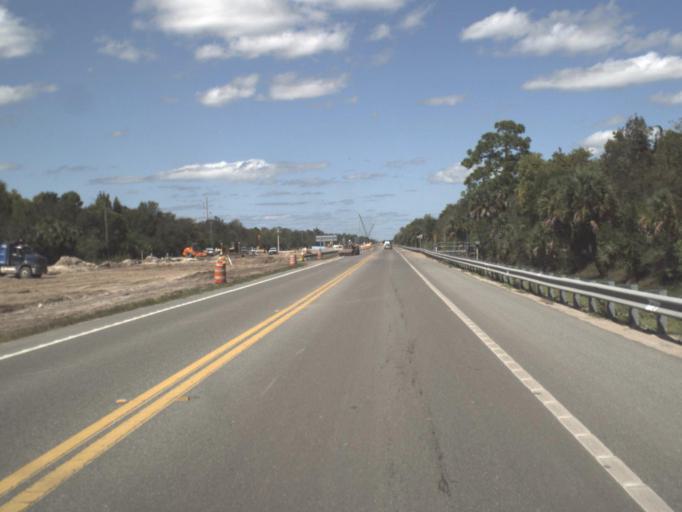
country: US
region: Florida
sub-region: Collier County
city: Lely Resort
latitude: 26.0506
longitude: -81.6790
